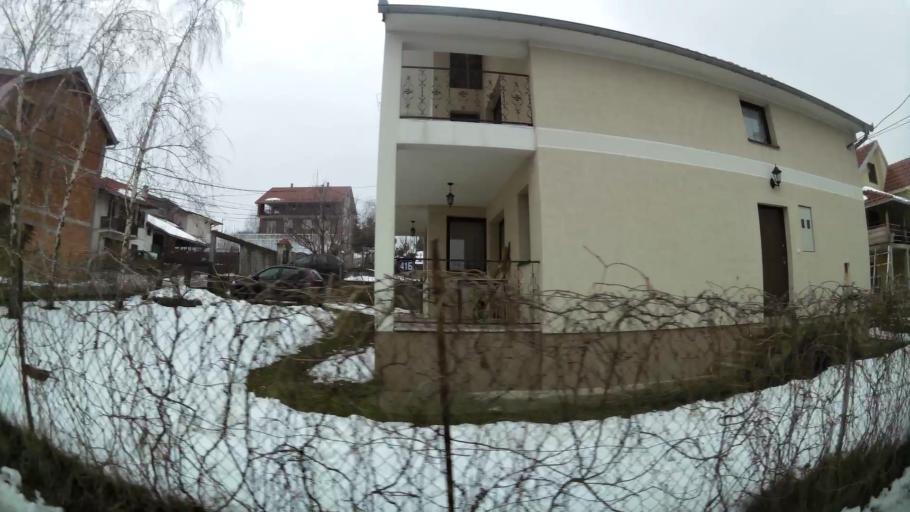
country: RS
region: Central Serbia
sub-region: Belgrade
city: Zvezdara
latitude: 44.7659
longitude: 20.5100
